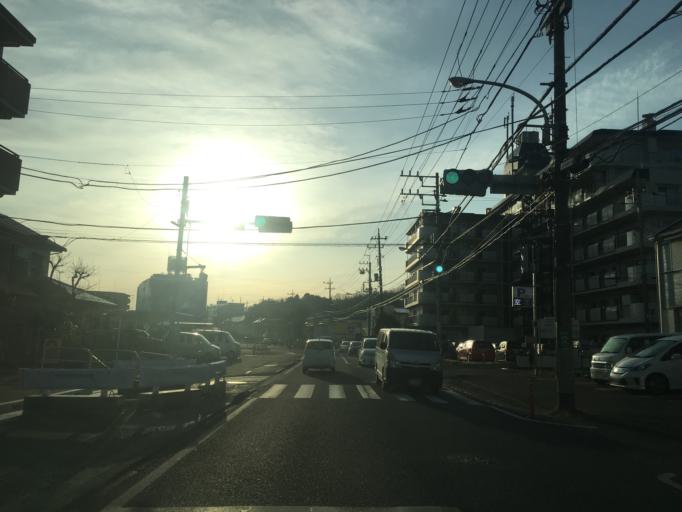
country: JP
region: Tokyo
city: Hino
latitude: 35.6576
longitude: 139.4267
